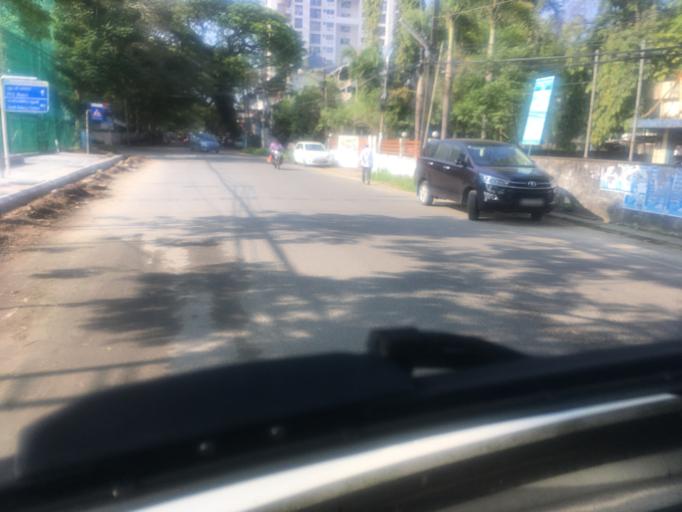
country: IN
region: Kerala
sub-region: Ernakulam
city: Cochin
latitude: 9.9702
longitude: 76.2978
